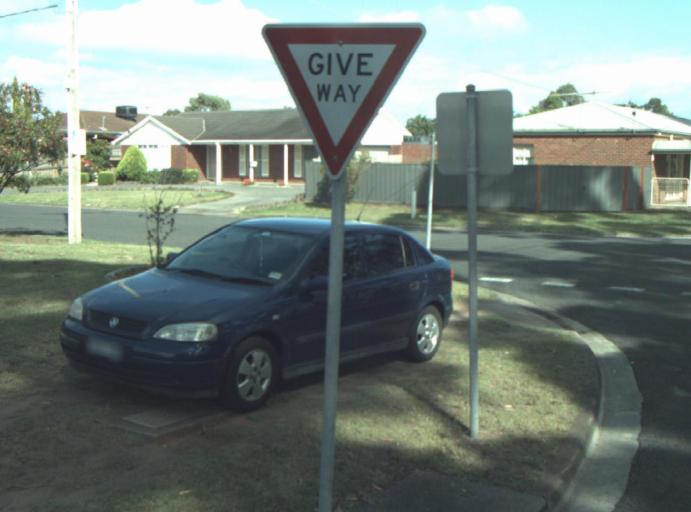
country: AU
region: Victoria
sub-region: Greater Geelong
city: Lara
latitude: -38.0191
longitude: 144.3924
